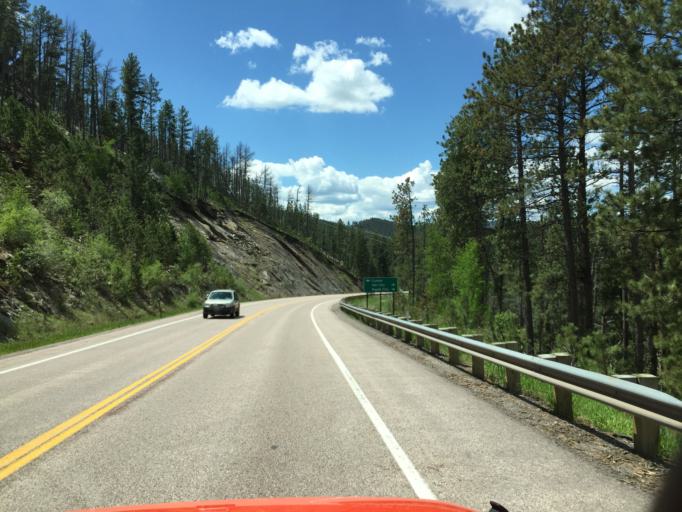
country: US
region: South Dakota
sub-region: Custer County
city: Custer
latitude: 43.8934
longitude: -103.5856
